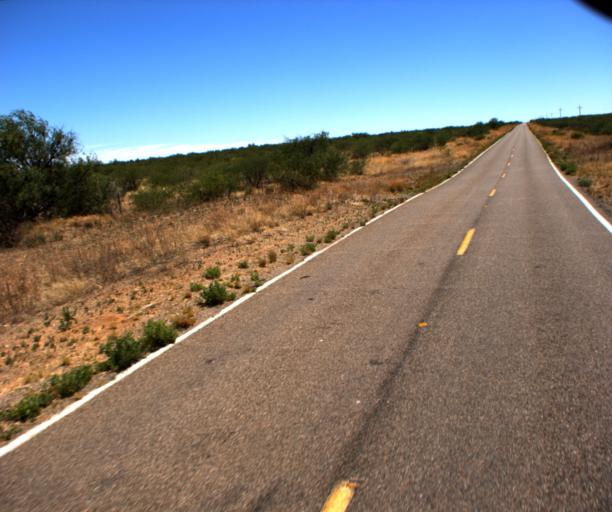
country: US
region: Arizona
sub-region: Pima County
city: Three Points
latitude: 31.7727
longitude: -111.4665
